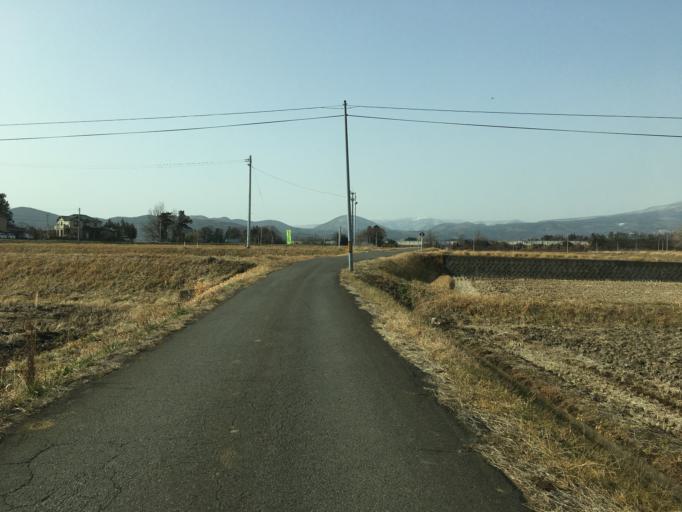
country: JP
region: Fukushima
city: Motomiya
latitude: 37.5342
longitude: 140.3908
